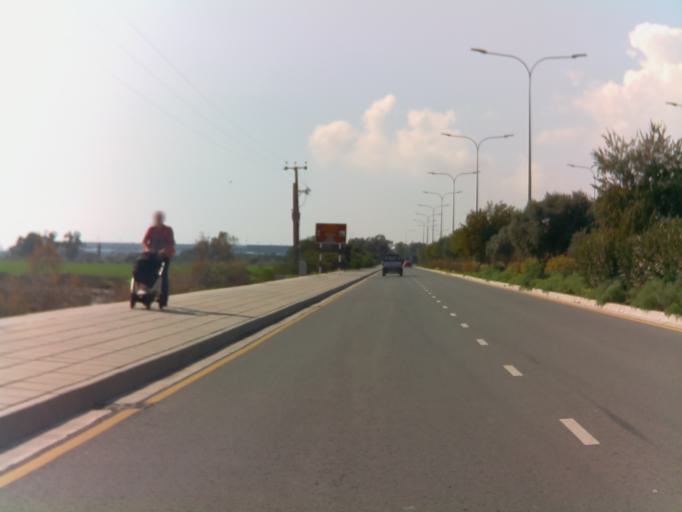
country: CY
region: Larnaka
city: Meneou
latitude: 34.8803
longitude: 33.6186
